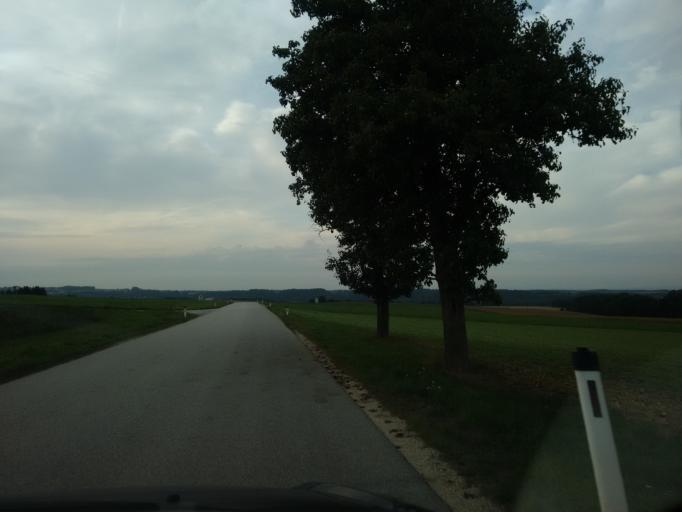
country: AT
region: Upper Austria
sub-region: Politischer Bezirk Steyr-Land
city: Pfarrkirchen bei Bad Hall
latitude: 48.0448
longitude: 14.1835
